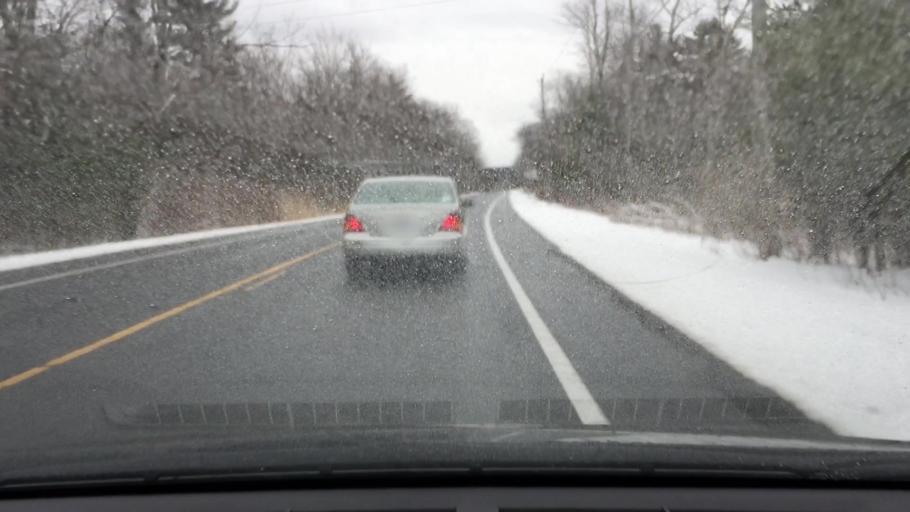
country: US
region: Massachusetts
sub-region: Hampshire County
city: Pelham
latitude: 42.3611
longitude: -72.3995
